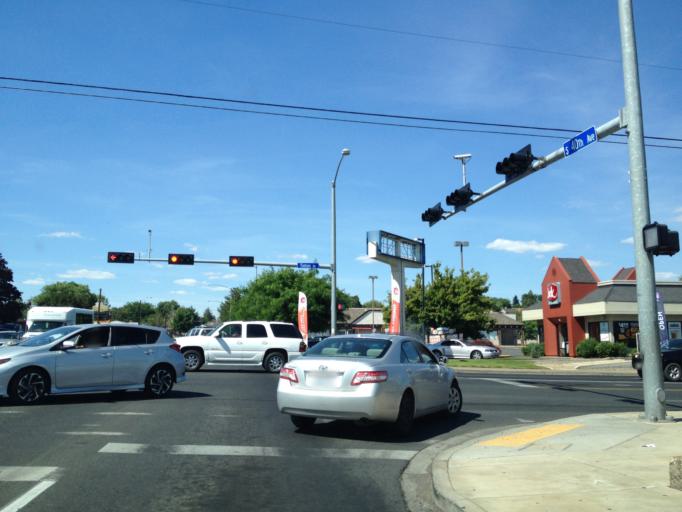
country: US
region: Washington
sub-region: Yakima County
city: West Valley
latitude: 46.5924
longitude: -120.5619
